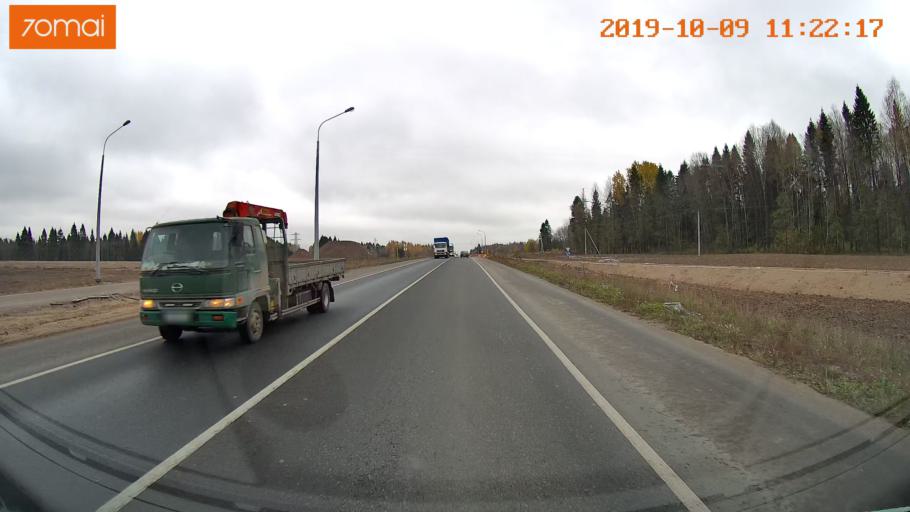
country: RU
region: Vologda
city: Vologda
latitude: 59.1329
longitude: 39.9566
